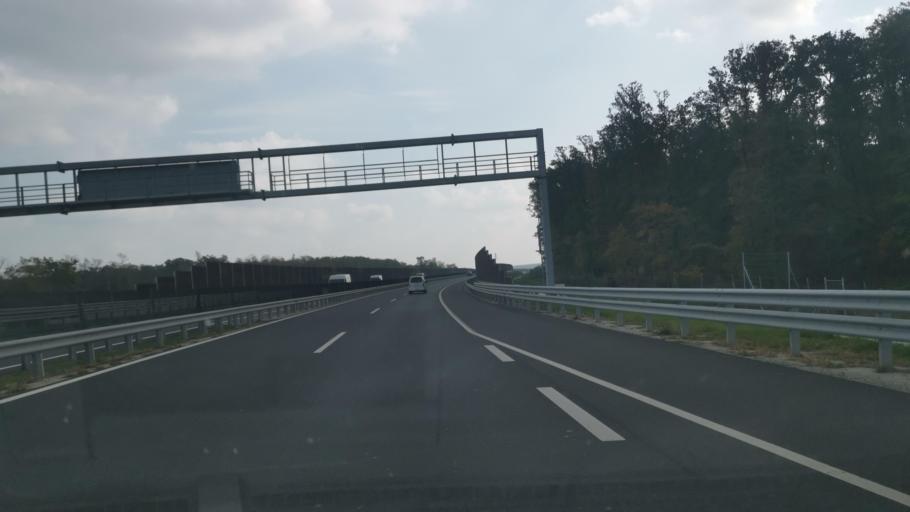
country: AT
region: Burgenland
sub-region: Politischer Bezirk Oberpullendorf
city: Deutschkreutz
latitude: 47.6255
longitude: 16.6516
